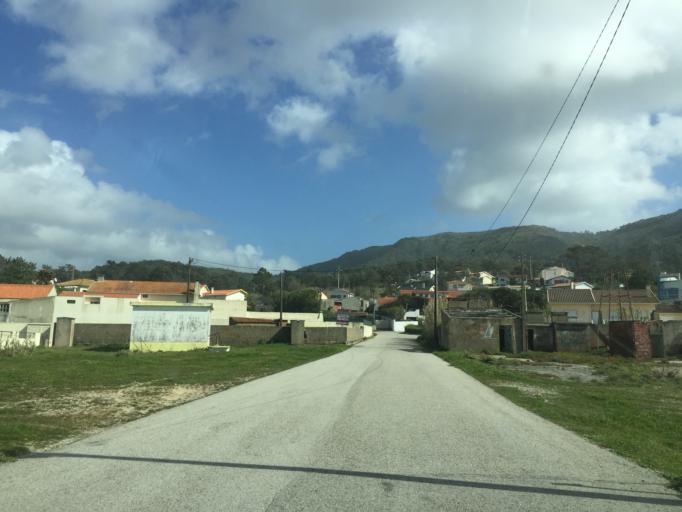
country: PT
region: Coimbra
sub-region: Figueira da Foz
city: Buarcos
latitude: 40.2091
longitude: -8.8960
